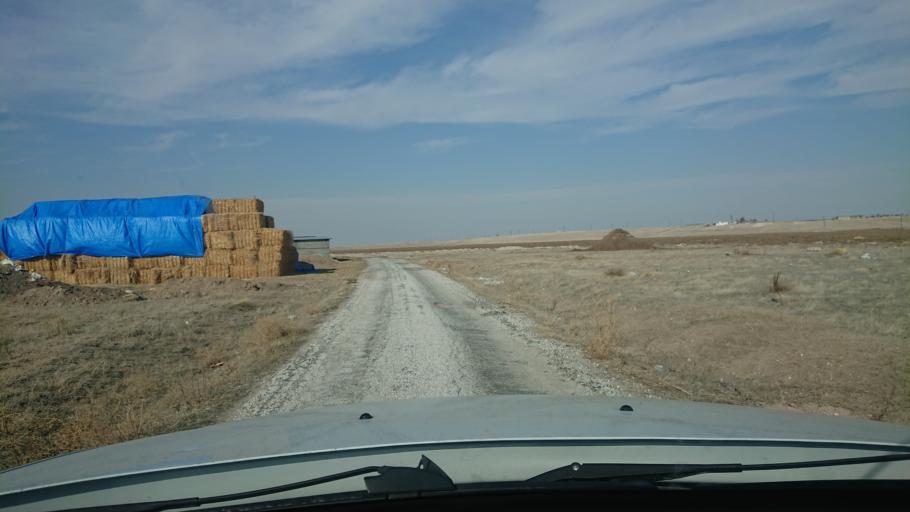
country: TR
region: Aksaray
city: Sultanhani
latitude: 38.2591
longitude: 33.4746
